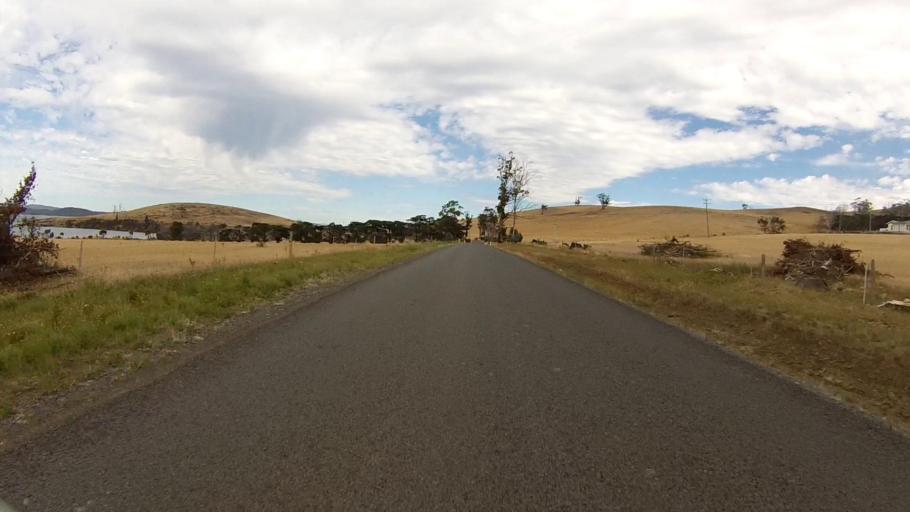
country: AU
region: Tasmania
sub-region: Sorell
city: Sorell
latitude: -42.8951
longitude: 147.7755
